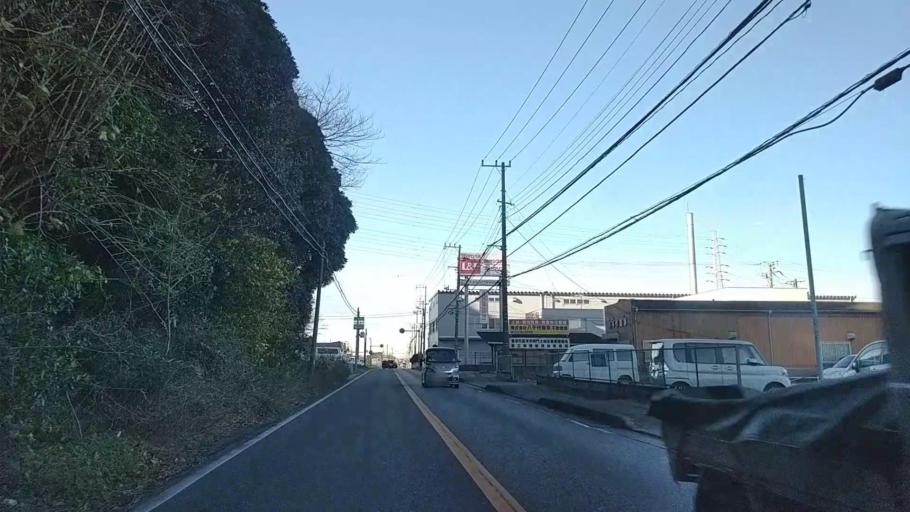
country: JP
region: Chiba
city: Kimitsu
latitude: 35.3425
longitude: 139.8739
